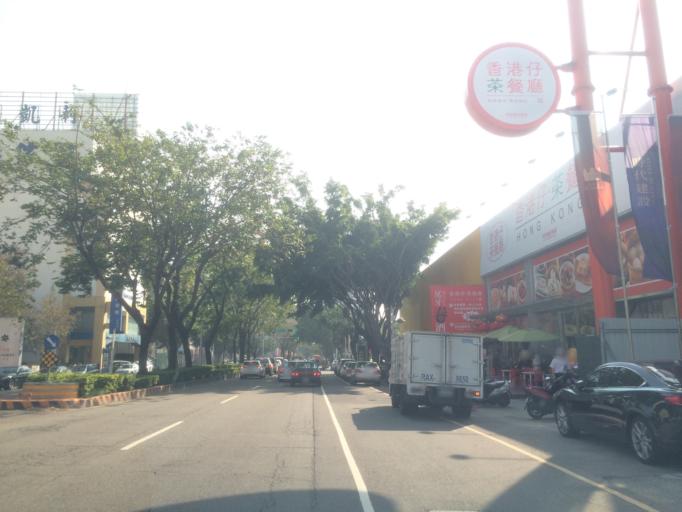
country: TW
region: Taiwan
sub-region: Taichung City
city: Taichung
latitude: 24.1848
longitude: 120.6862
